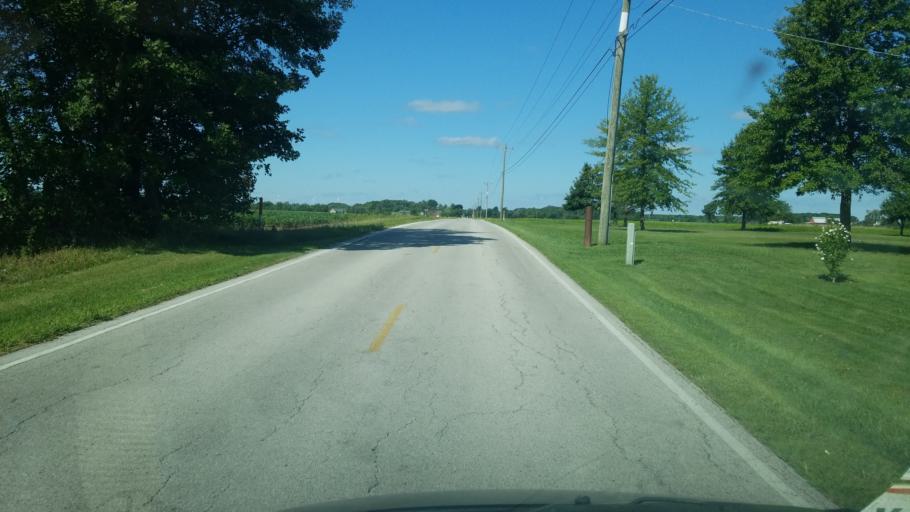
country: US
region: Ohio
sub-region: Hancock County
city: Findlay
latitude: 41.1092
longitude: -83.5830
